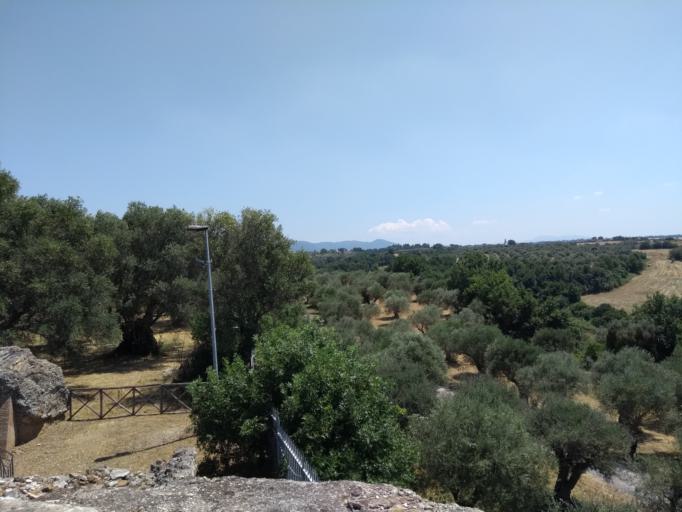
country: IT
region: Latium
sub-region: Citta metropolitana di Roma Capitale
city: Villa Adriana
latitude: 41.9378
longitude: 12.7730
